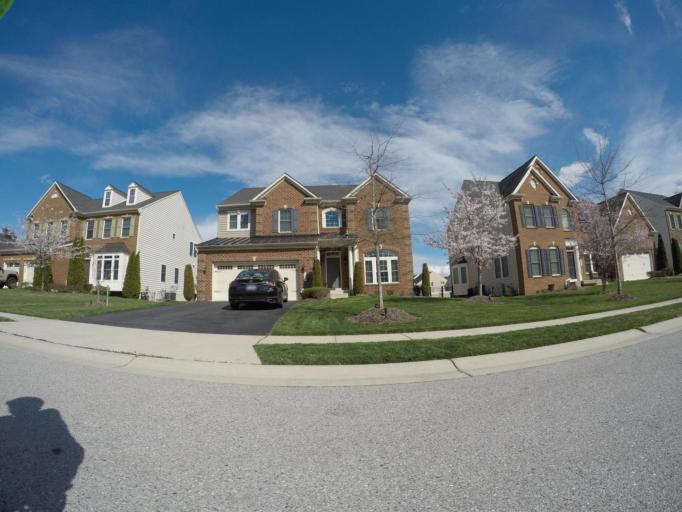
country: US
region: Maryland
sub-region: Anne Arundel County
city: Pasadena
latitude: 39.0949
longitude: -76.5674
